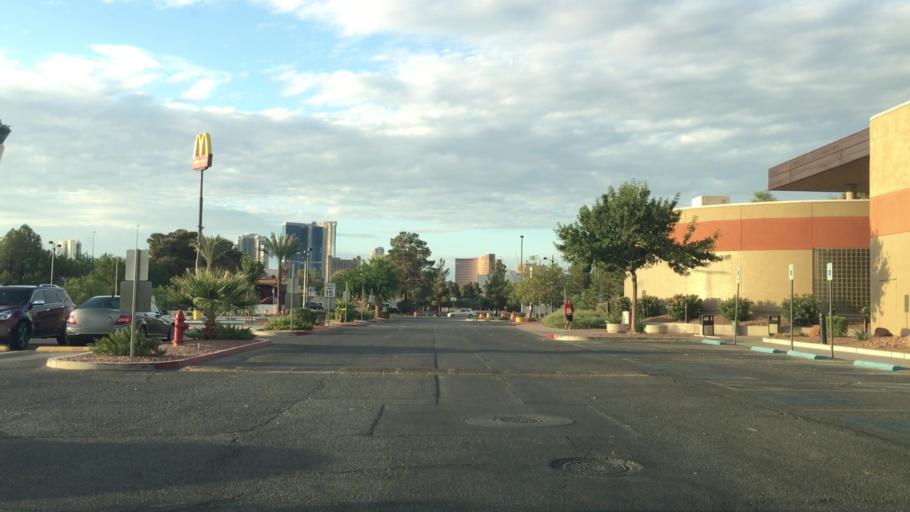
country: US
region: Nevada
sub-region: Clark County
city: Las Vegas
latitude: 36.1602
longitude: -115.1630
